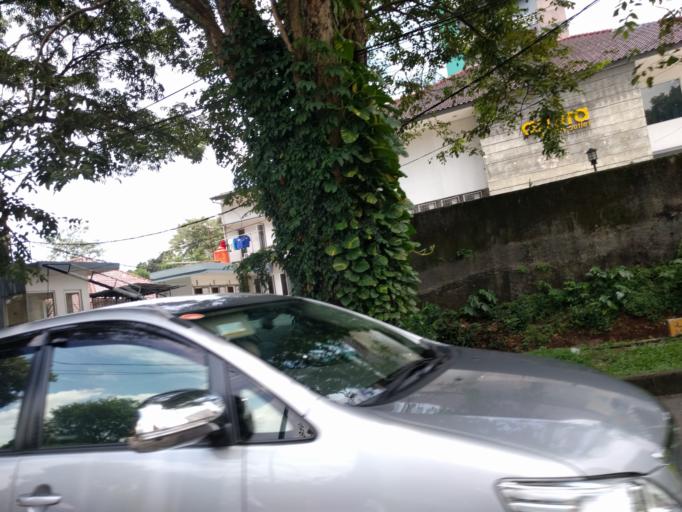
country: ID
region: West Java
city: Bogor
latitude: -6.5887
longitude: 106.8053
